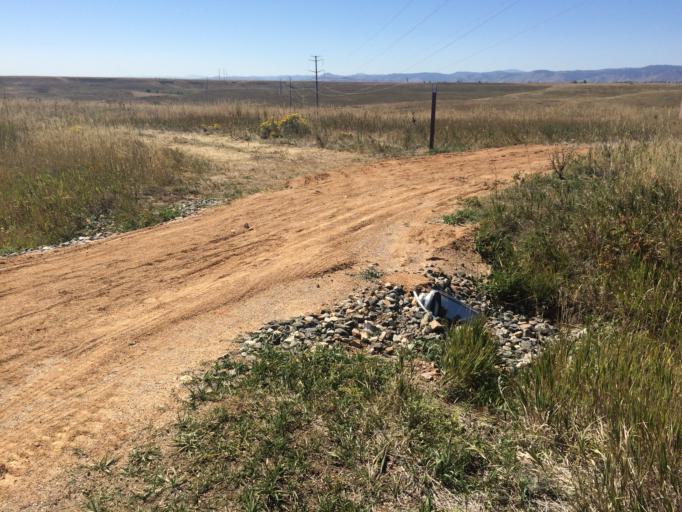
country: US
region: Colorado
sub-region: Boulder County
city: Superior
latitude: 39.9108
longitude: -105.1839
